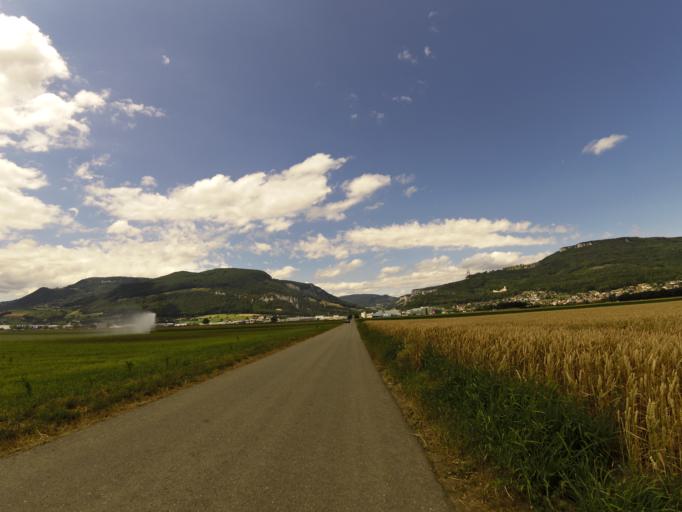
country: CH
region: Solothurn
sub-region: Bezirk Gaeu
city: Oensingen
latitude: 47.2743
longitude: 7.7284
